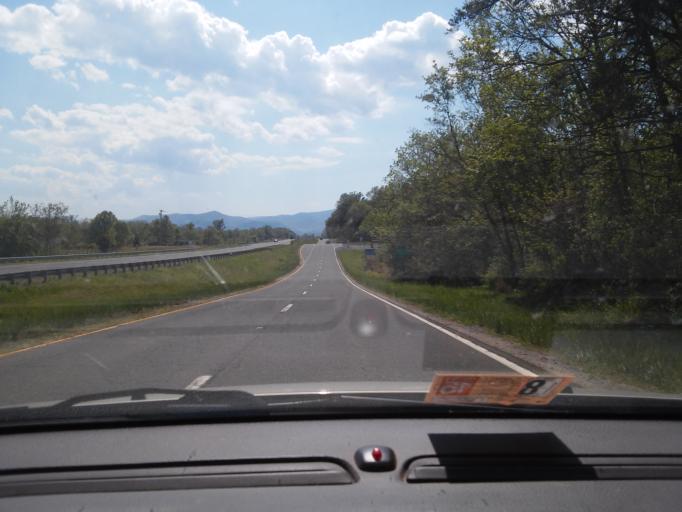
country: US
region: Virginia
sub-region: Rappahannock County
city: Washington
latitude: 38.6954
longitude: -78.1677
